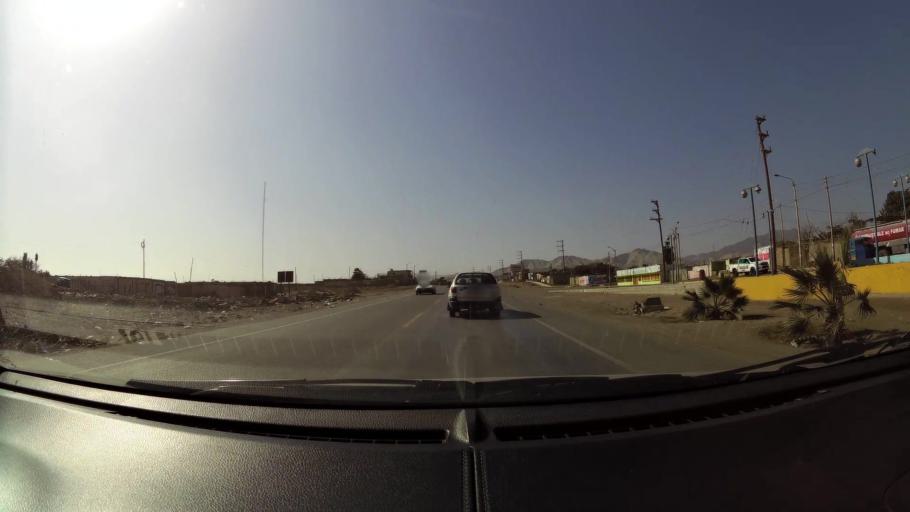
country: PE
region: Ancash
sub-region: Provincia de Huarmey
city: Huarmey
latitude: -10.0515
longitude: -78.1584
